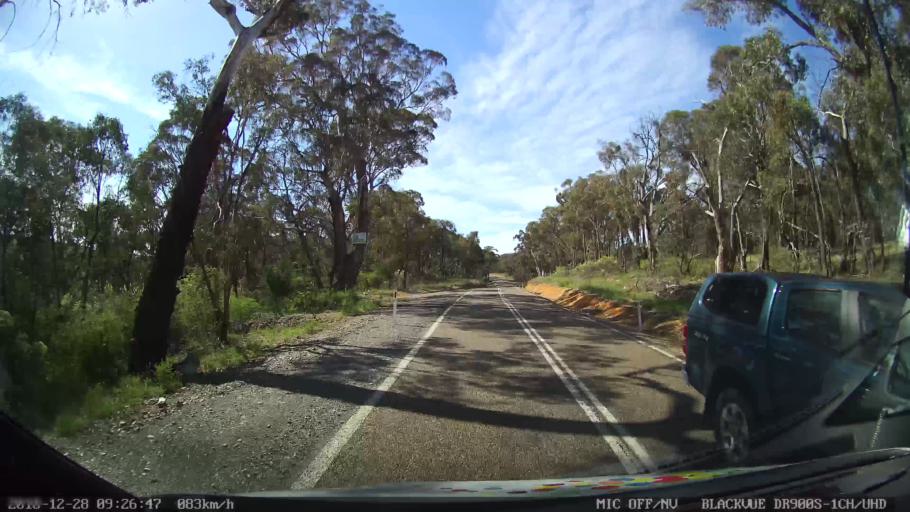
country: AU
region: New South Wales
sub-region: Upper Lachlan Shire
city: Crookwell
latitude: -34.4221
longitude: 149.4040
